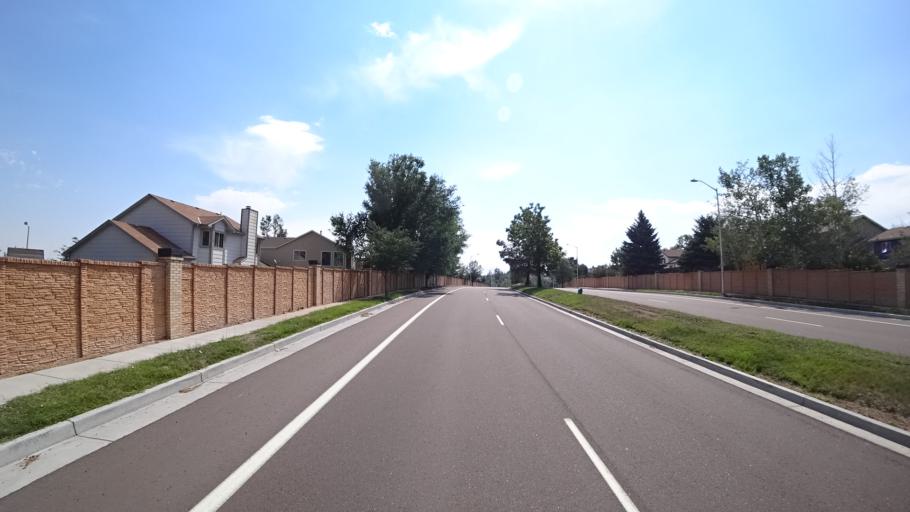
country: US
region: Colorado
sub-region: El Paso County
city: Cimarron Hills
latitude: 38.9254
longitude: -104.7638
